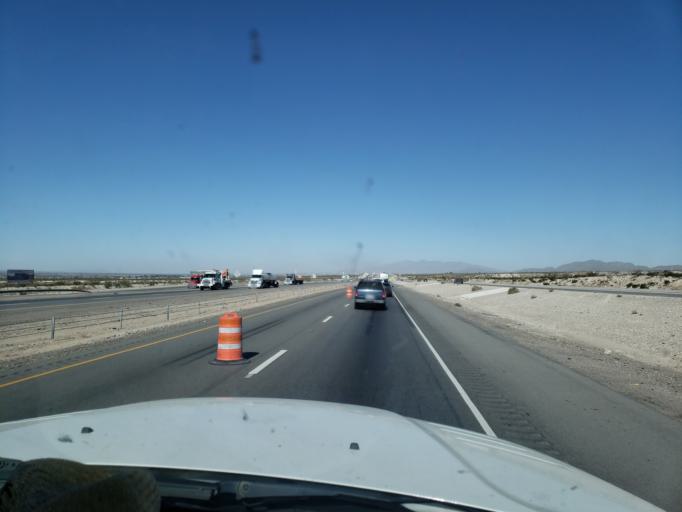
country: US
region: Texas
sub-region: El Paso County
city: Canutillo
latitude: 31.9258
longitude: -106.5827
